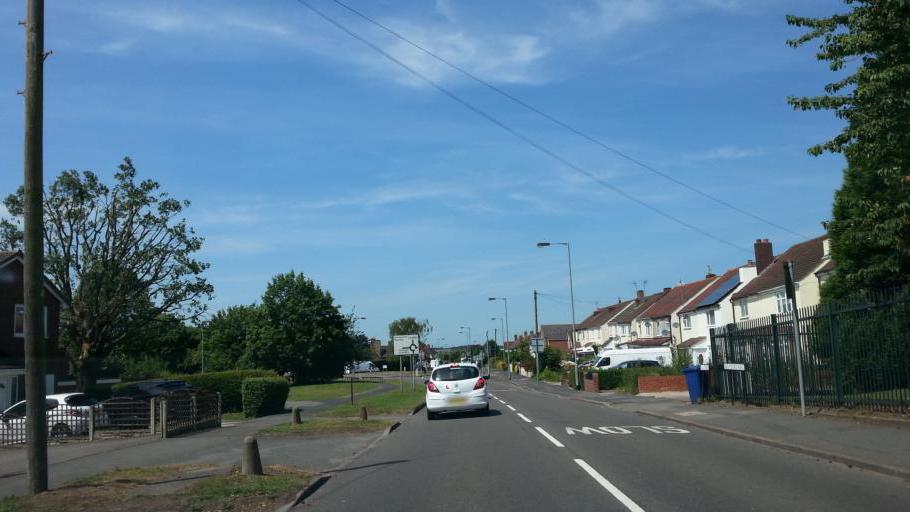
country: GB
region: England
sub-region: Staffordshire
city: Norton Canes
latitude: 52.6932
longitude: -1.9883
